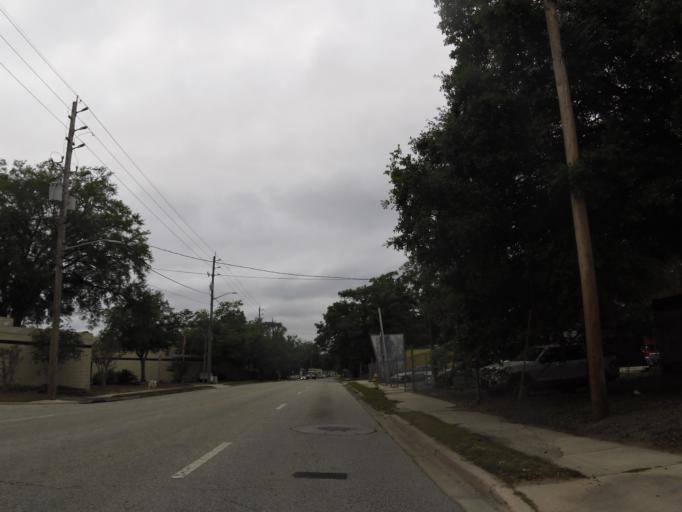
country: US
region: Florida
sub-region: Duval County
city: Jacksonville
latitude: 30.2758
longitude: -81.6414
